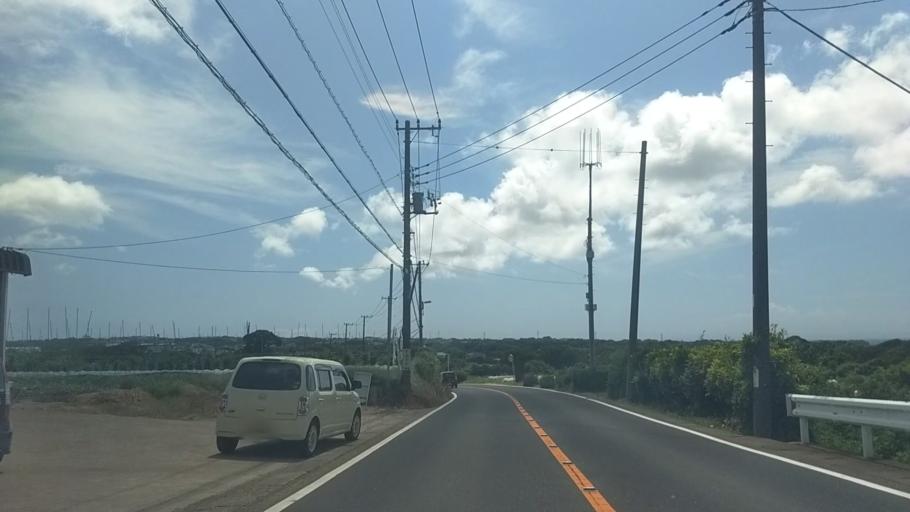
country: JP
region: Kanagawa
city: Miura
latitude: 35.1947
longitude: 139.6490
